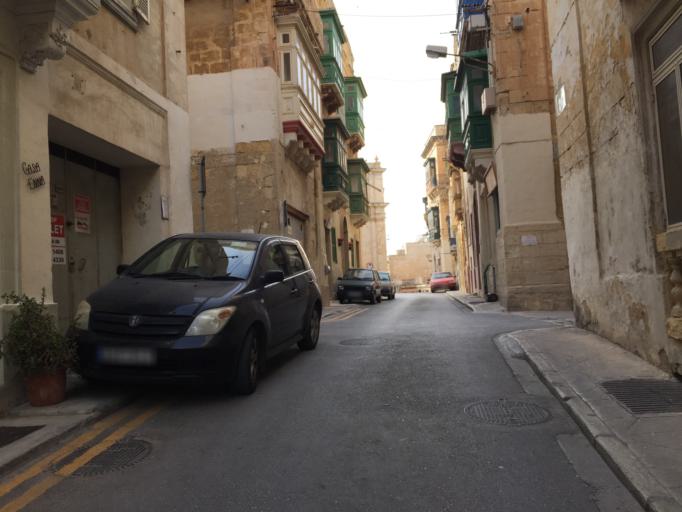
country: MT
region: L-Isla
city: Senglea
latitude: 35.8893
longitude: 14.5160
